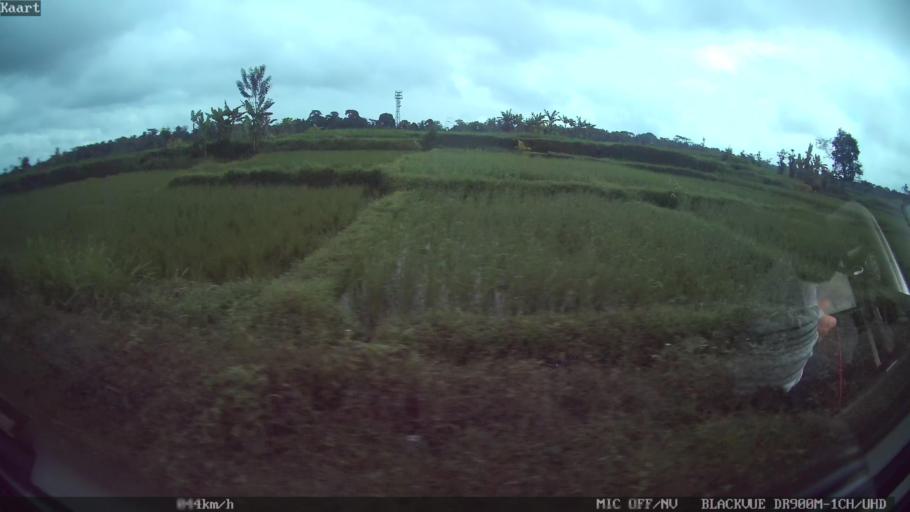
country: ID
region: Bali
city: Banjar Teguan
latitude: -8.4969
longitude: 115.2257
